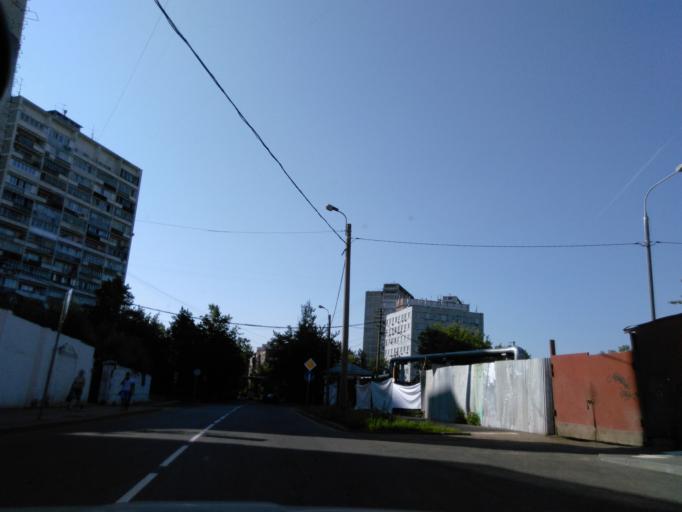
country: RU
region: Moskovskaya
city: Dorogomilovo
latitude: 55.7798
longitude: 37.5700
